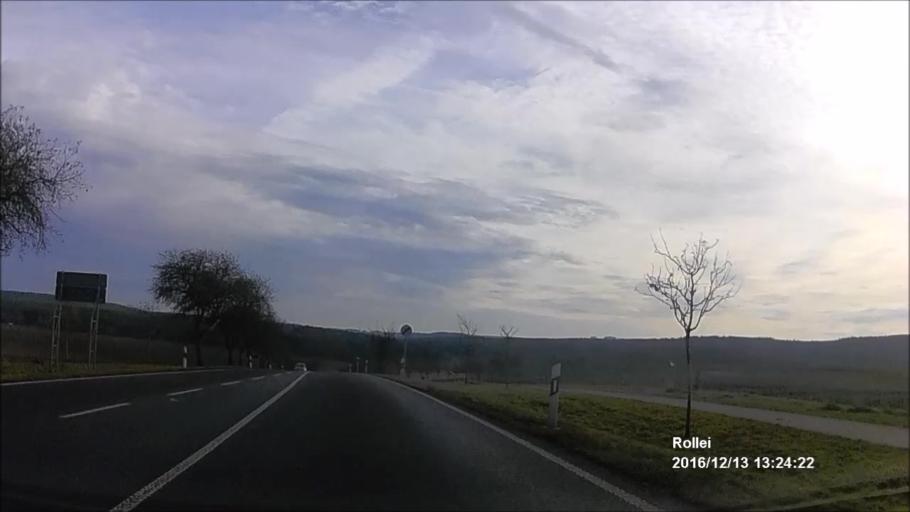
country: DE
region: Thuringia
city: Nauendorf
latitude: 50.8843
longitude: 11.1818
